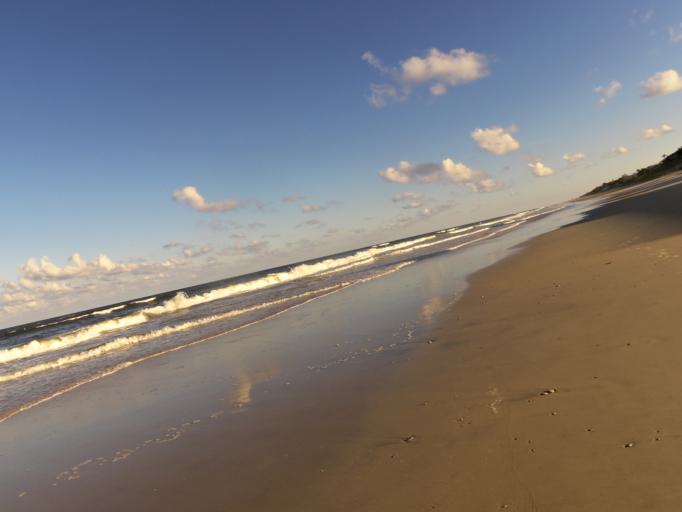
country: US
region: Florida
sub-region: Saint Johns County
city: Sawgrass
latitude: 30.1797
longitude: -81.3601
